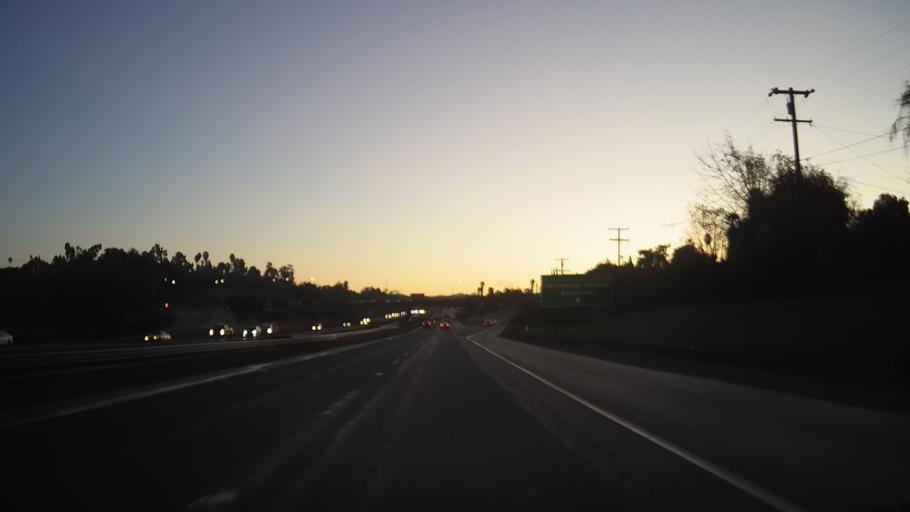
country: US
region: California
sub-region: San Diego County
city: Spring Valley
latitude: 32.7438
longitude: -116.9801
